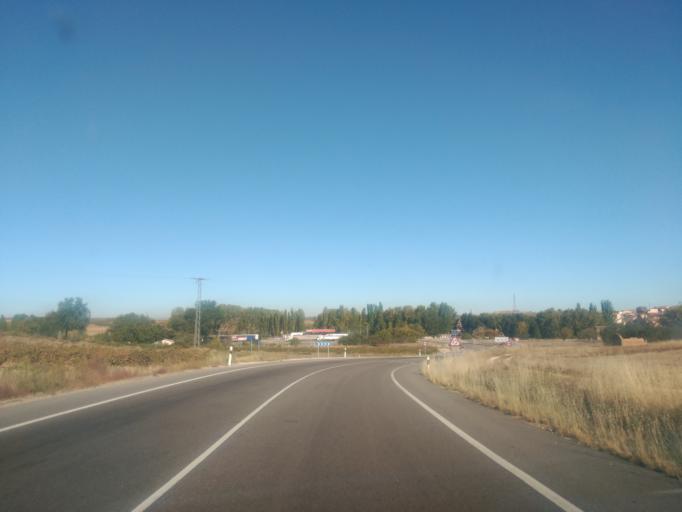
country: ES
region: Castille and Leon
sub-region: Provincia de Burgos
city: Castrillo de la Vega
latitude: 41.6457
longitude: -3.7809
